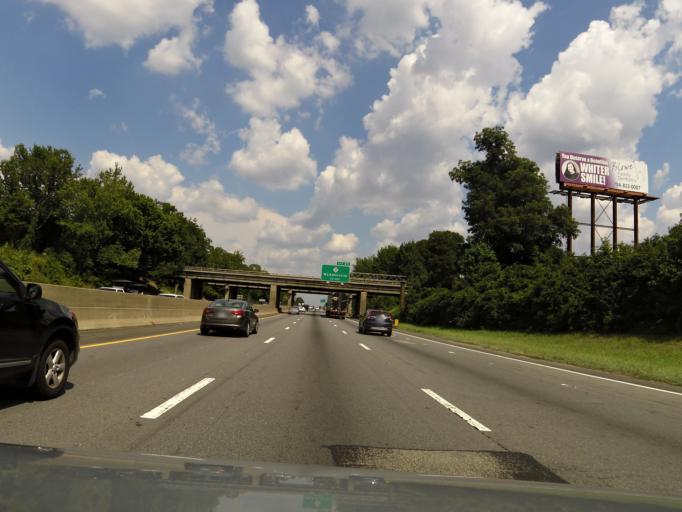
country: US
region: North Carolina
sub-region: Gaston County
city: Lowell
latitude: 35.2606
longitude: -81.0998
